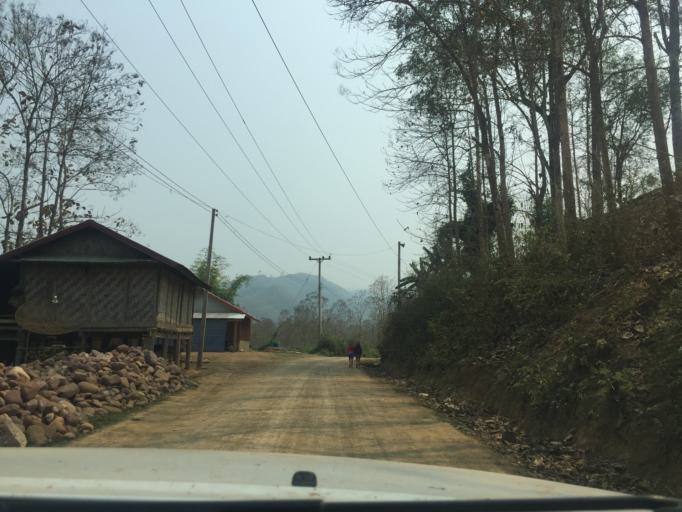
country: LA
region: Loungnamtha
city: Muang Nale
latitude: 20.3030
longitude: 101.6505
